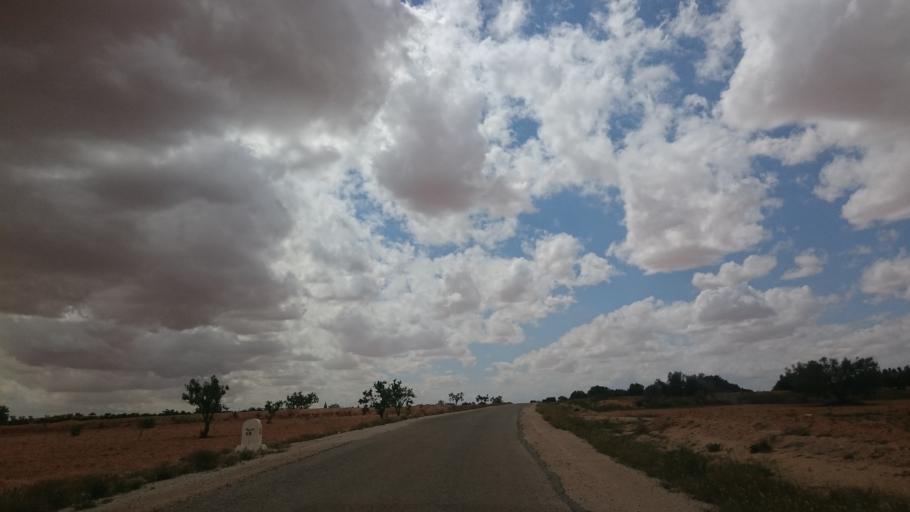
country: TN
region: Safaqis
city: Bi'r `Ali Bin Khalifah
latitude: 34.7808
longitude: 10.3869
